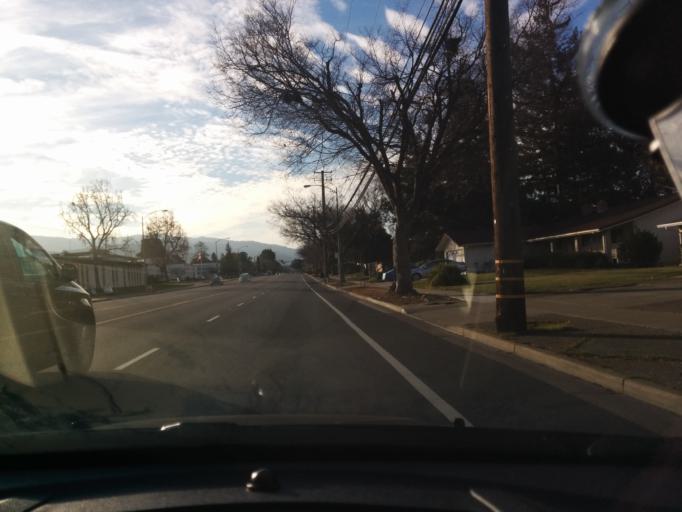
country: US
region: California
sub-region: Santa Clara County
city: Cupertino
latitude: 37.3376
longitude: -122.0468
